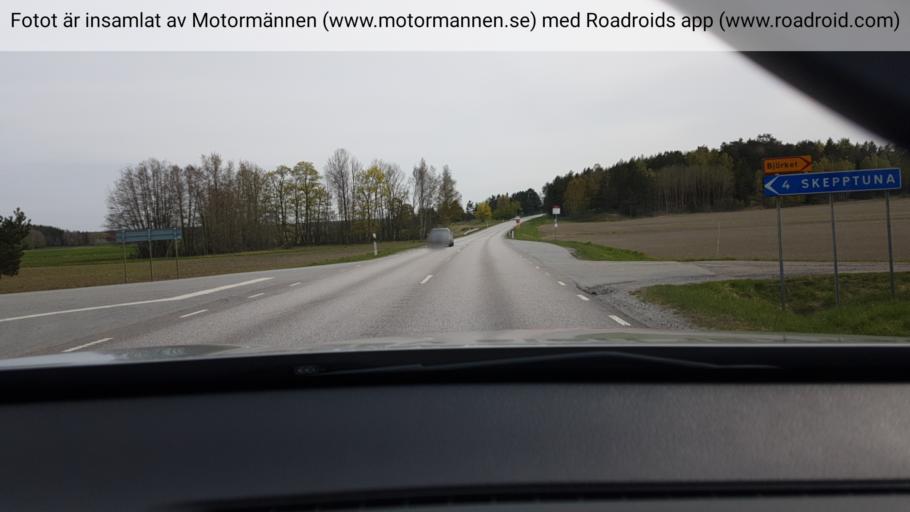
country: SE
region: Stockholm
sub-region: Vallentuna Kommun
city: Vallentuna
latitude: 59.6938
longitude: 18.0449
